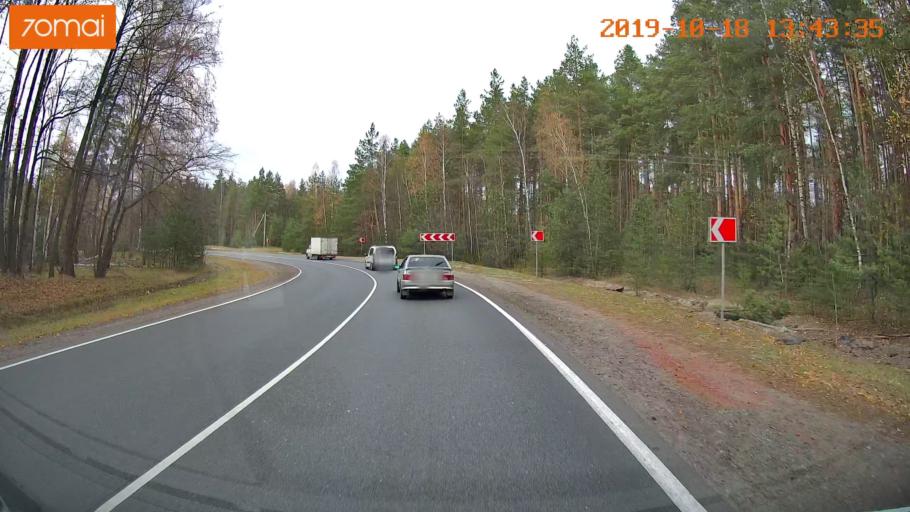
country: RU
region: Rjazan
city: Solotcha
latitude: 54.9314
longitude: 39.9742
